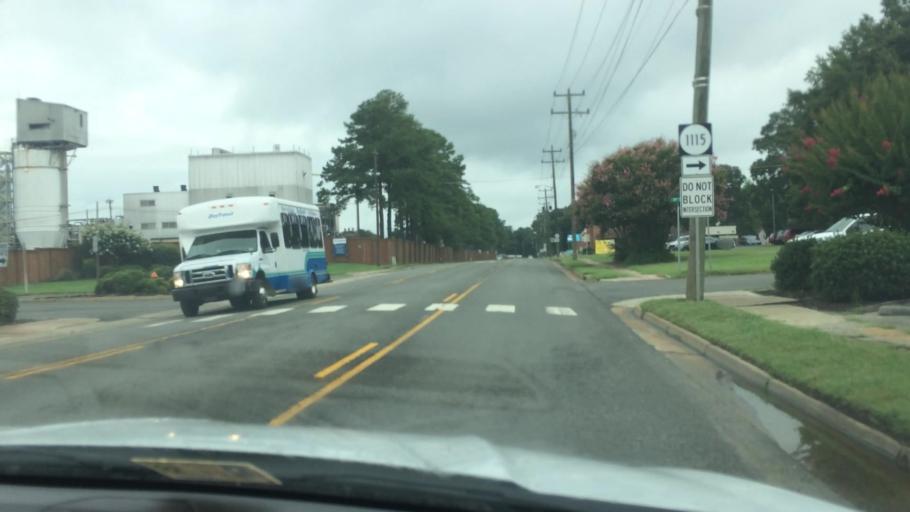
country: US
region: Virginia
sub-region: King William County
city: West Point
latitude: 37.5404
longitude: -76.8012
